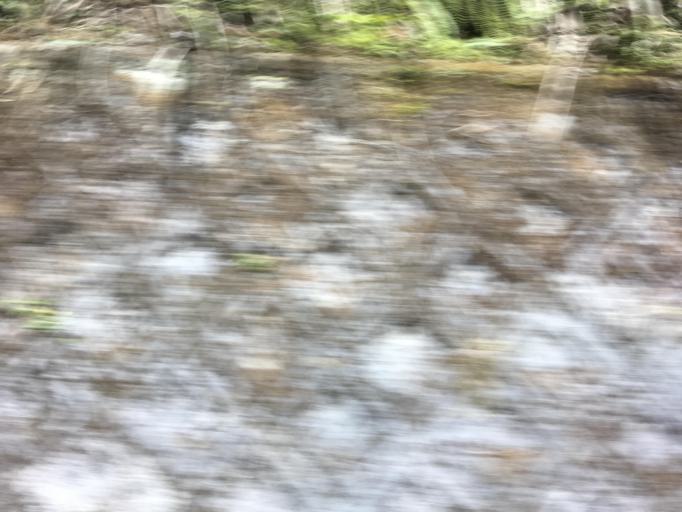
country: TW
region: Taiwan
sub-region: Yilan
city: Yilan
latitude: 24.5331
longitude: 121.5212
